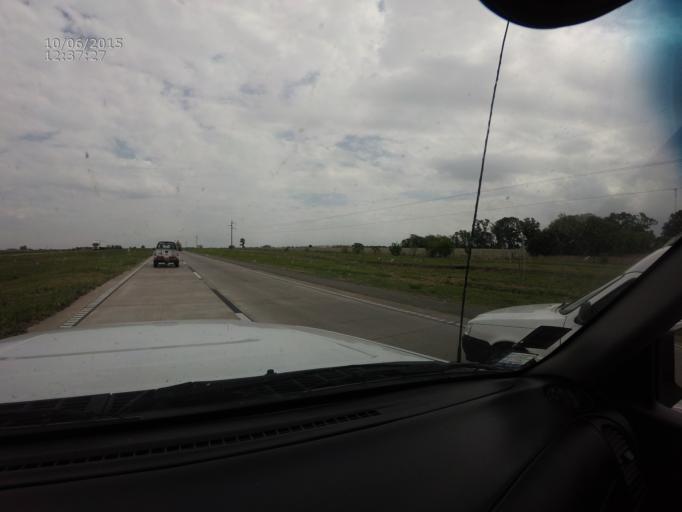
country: AR
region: Santa Fe
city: Carcarana
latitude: -32.8684
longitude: -61.2202
